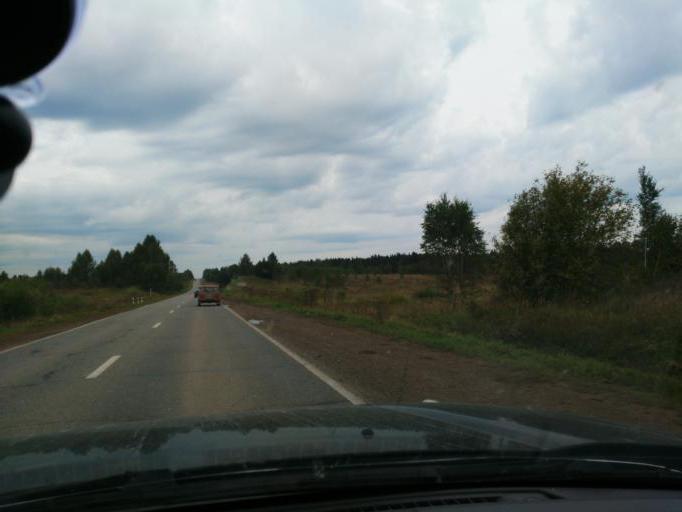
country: RU
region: Perm
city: Chernushka
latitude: 56.7478
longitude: 56.1562
